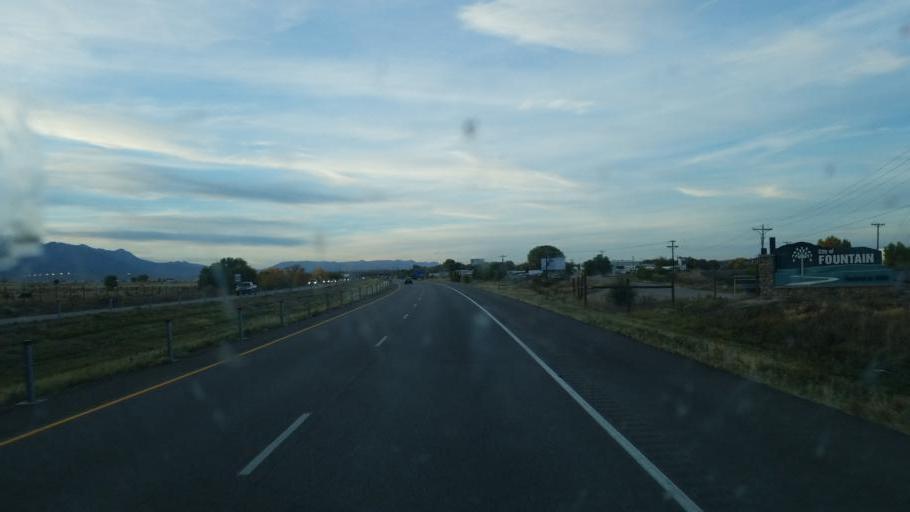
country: US
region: Colorado
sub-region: El Paso County
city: Fountain
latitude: 38.6635
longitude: -104.7017
